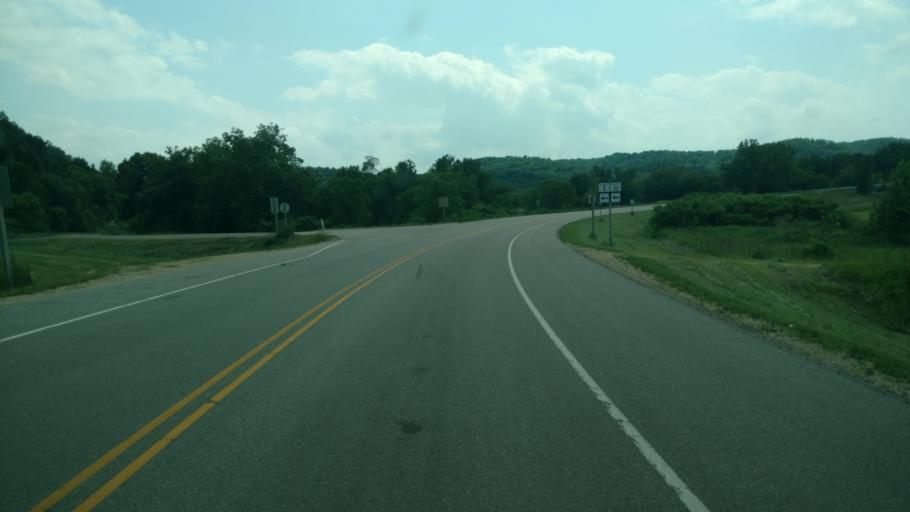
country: US
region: Wisconsin
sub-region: Vernon County
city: Viroqua
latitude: 43.4746
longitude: -90.6911
